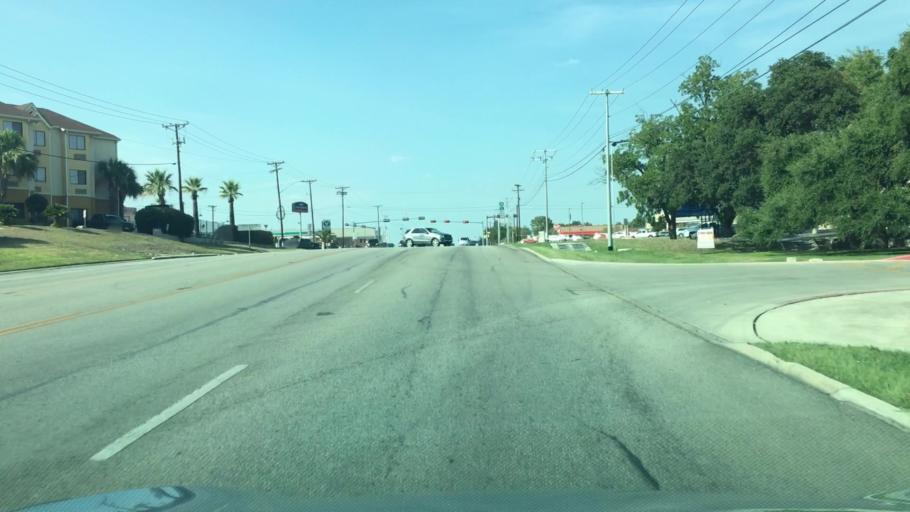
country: US
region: Texas
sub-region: Comal County
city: New Braunfels
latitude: 29.7008
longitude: -98.0971
